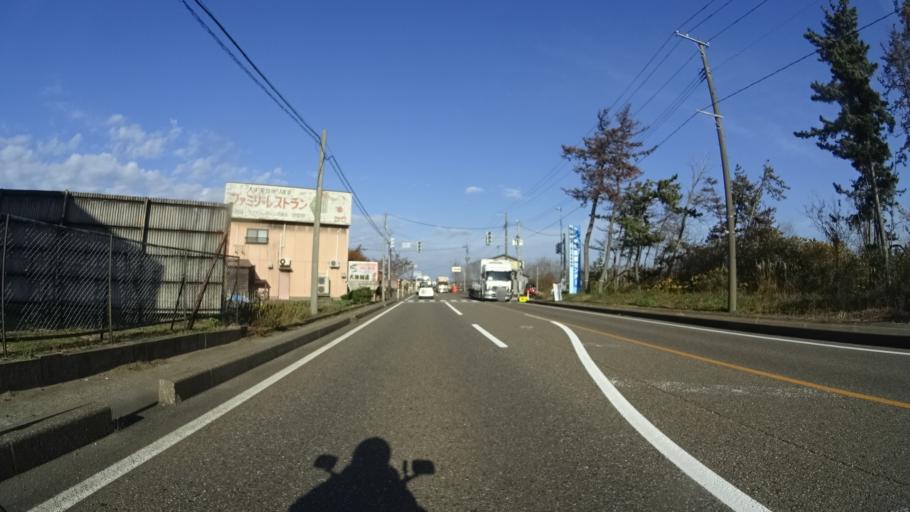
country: JP
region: Niigata
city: Joetsu
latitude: 37.2123
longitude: 138.3074
